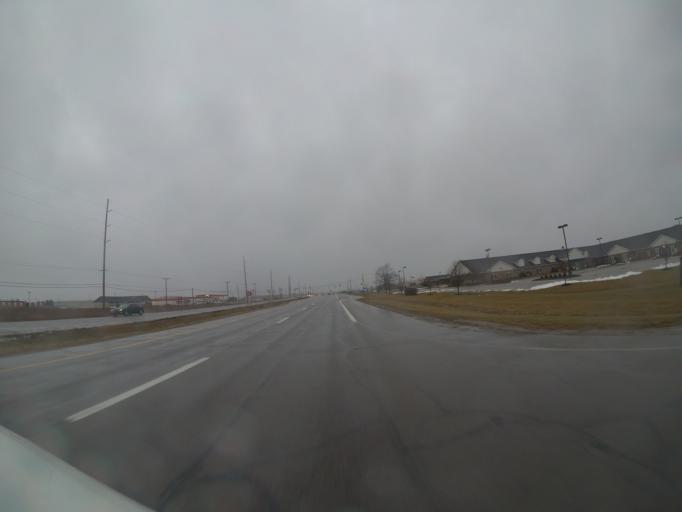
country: US
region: Ohio
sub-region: Wood County
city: Walbridge
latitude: 41.5639
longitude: -83.5351
